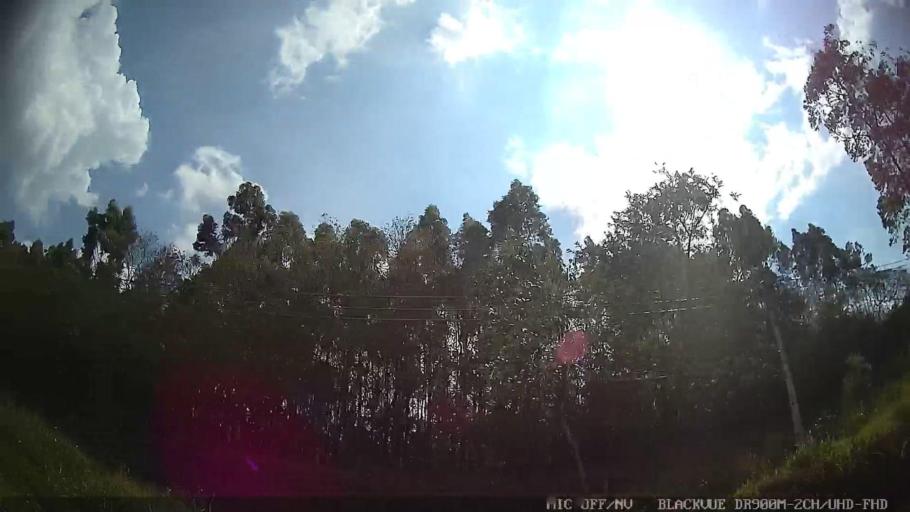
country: BR
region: Sao Paulo
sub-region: Braganca Paulista
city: Braganca Paulista
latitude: -22.9650
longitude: -46.5838
